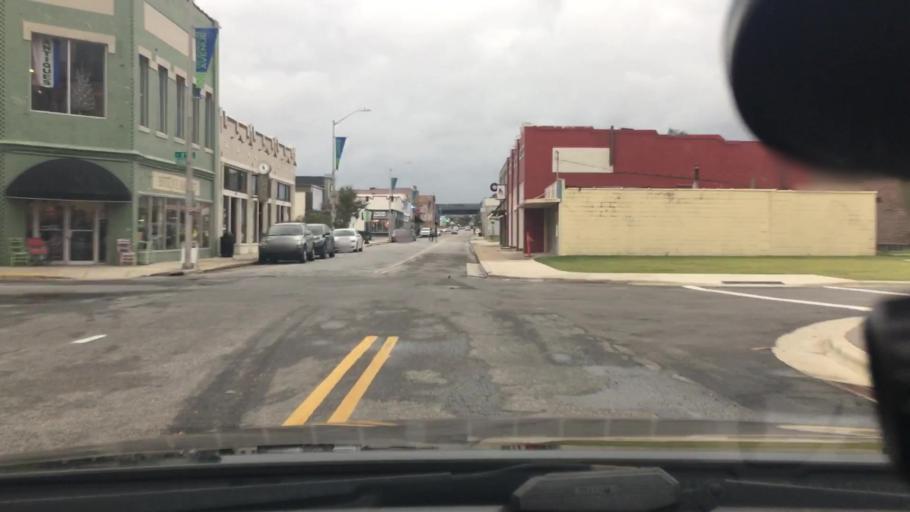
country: US
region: North Carolina
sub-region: Pitt County
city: Greenville
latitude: 35.6097
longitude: -77.3759
